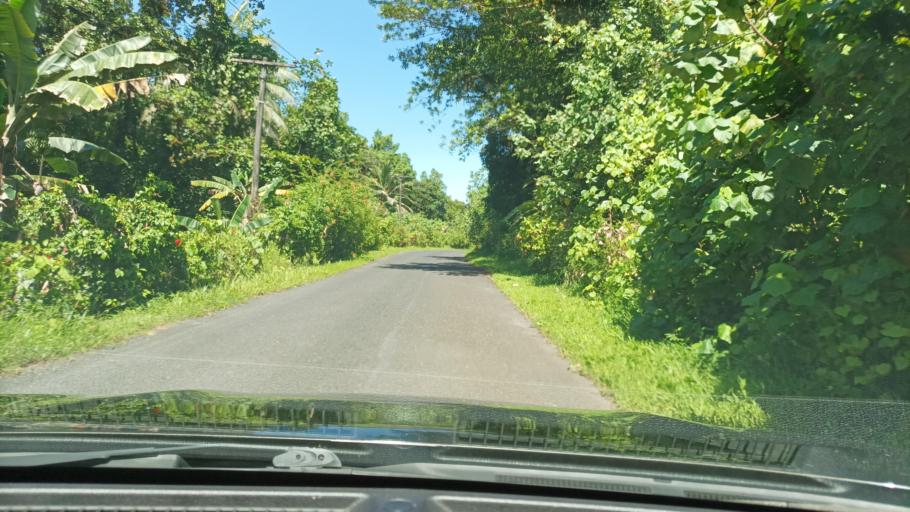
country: FM
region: Pohnpei
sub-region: Madolenihm Municipality
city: Madolenihm Municipality Government
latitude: 6.8659
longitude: 158.2898
